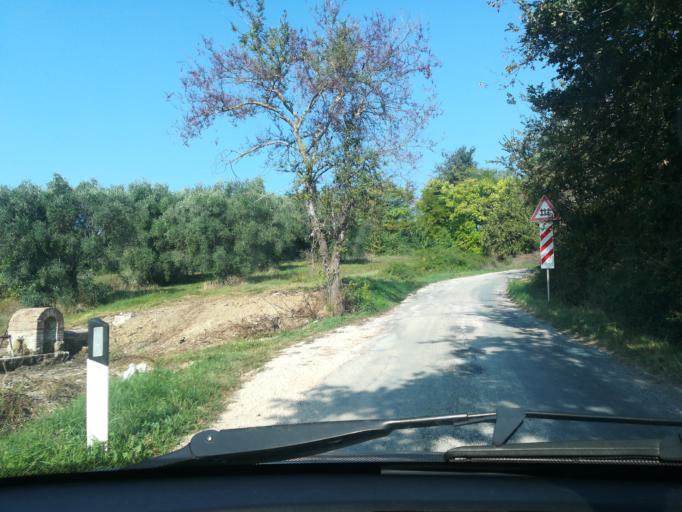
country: IT
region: The Marches
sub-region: Provincia di Macerata
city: Piediripa
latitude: 43.2741
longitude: 13.4668
